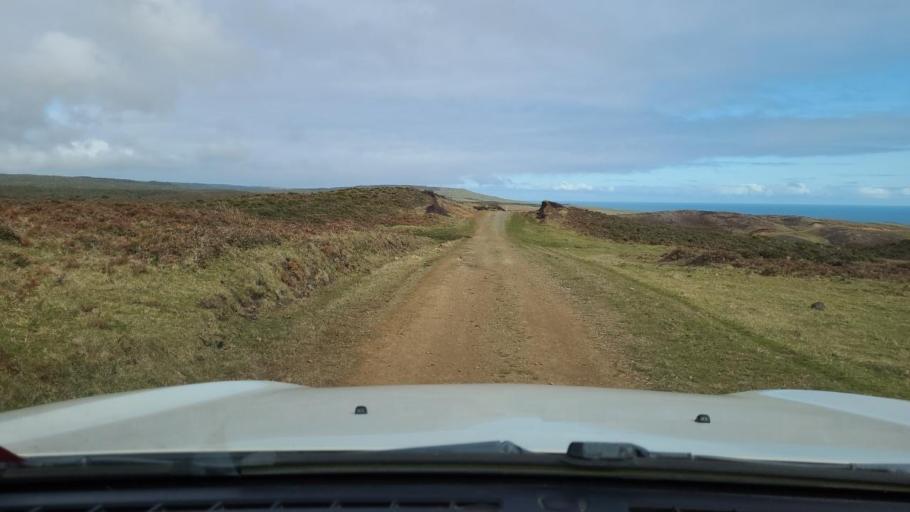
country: NZ
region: Chatham Islands
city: Waitangi
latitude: -44.0529
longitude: -176.6331
